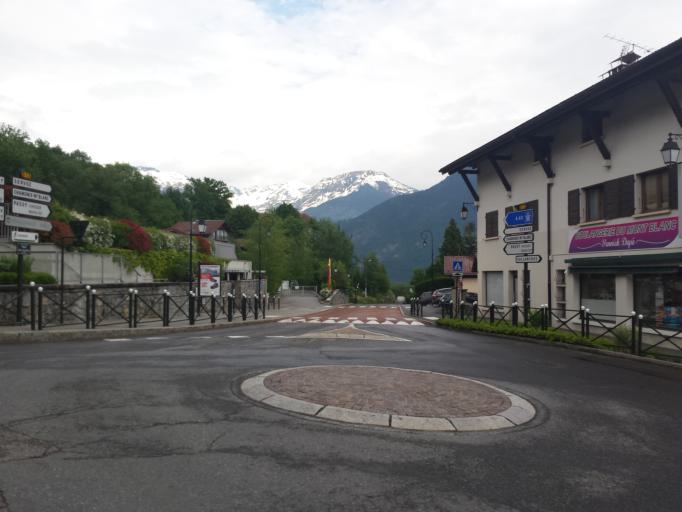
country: FR
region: Rhone-Alpes
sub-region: Departement de la Haute-Savoie
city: Passy
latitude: 45.9235
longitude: 6.6860
